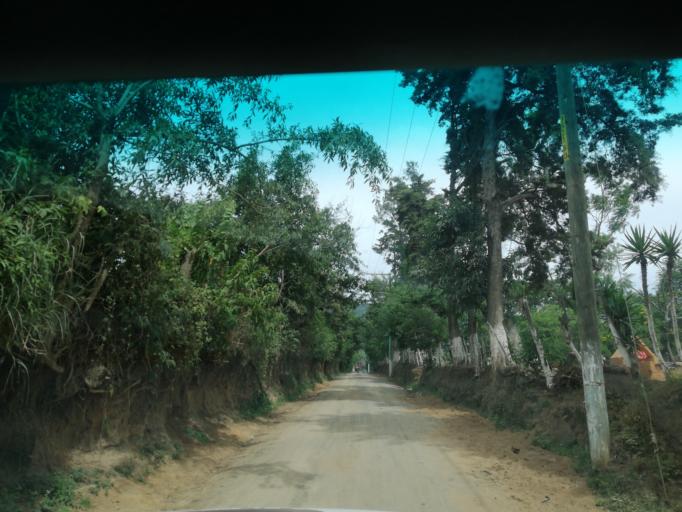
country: GT
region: Guatemala
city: Villa Nueva
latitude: 14.5362
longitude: -90.6281
